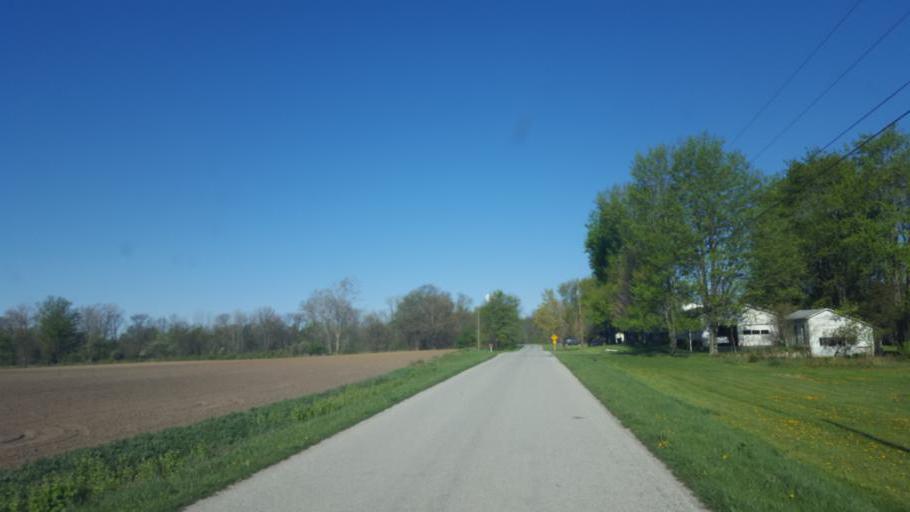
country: US
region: Ohio
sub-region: Morrow County
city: Cardington
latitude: 40.6380
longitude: -82.9609
